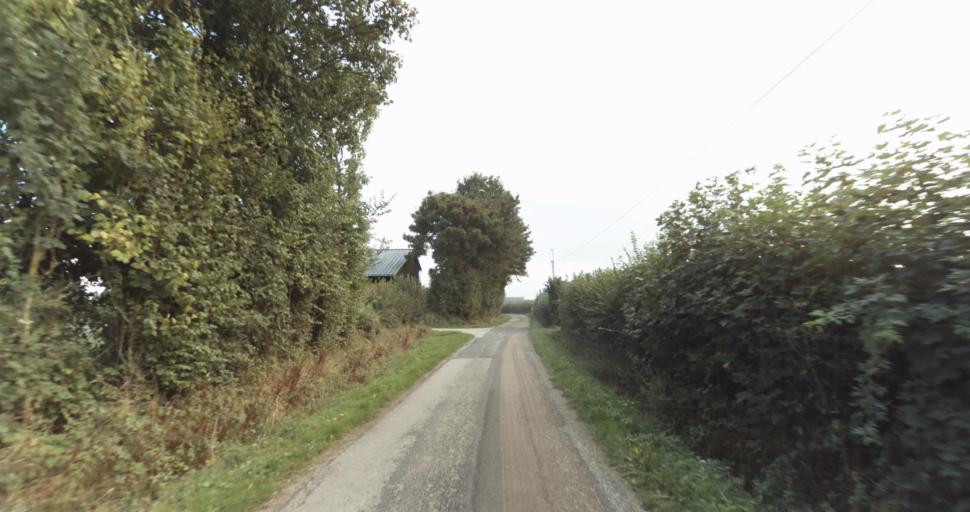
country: FR
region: Lower Normandy
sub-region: Departement de l'Orne
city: Gace
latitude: 48.7608
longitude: 0.3576
